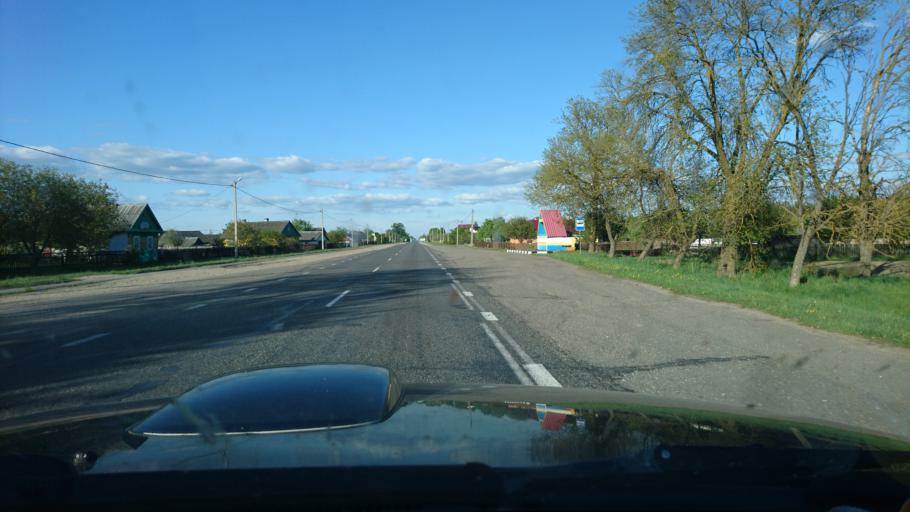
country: BY
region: Brest
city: Ivatsevichy
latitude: 52.6947
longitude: 25.3084
